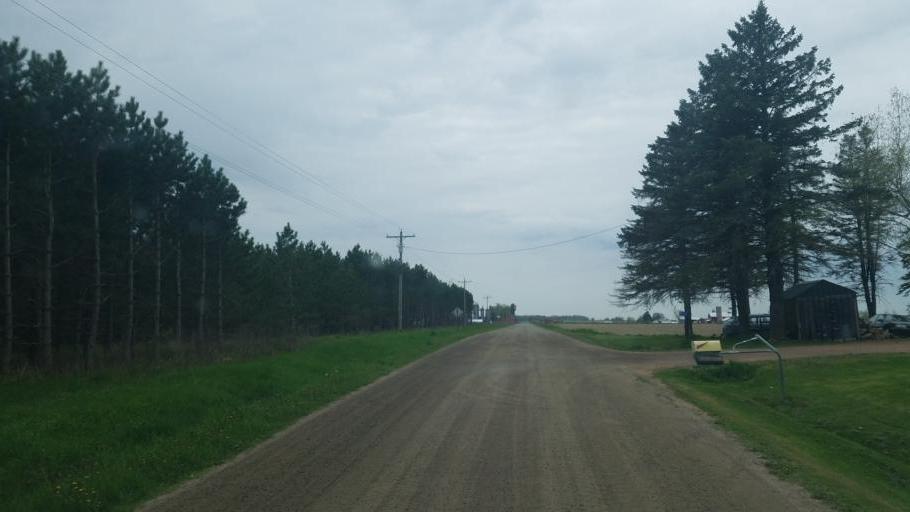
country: US
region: Wisconsin
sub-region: Clark County
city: Loyal
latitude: 44.6613
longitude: -90.4199
